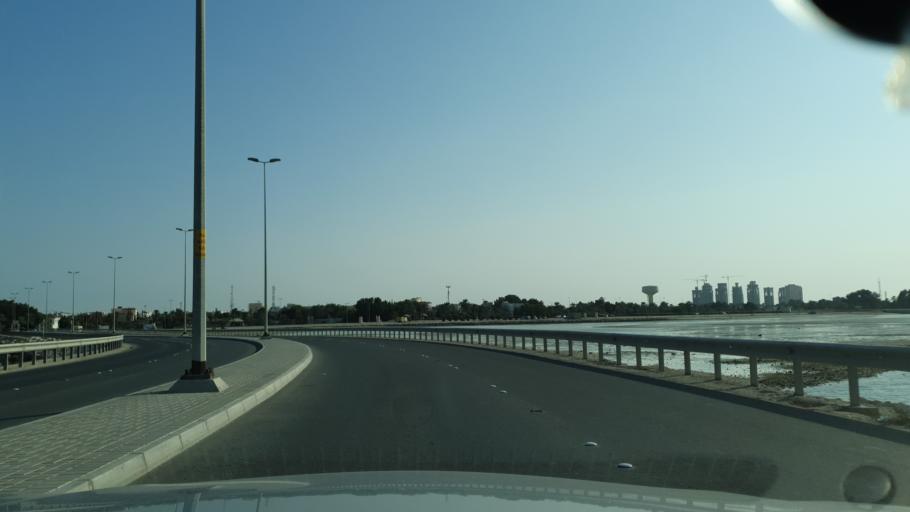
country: BH
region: Manama
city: Jidd Hafs
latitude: 26.2270
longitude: 50.4571
